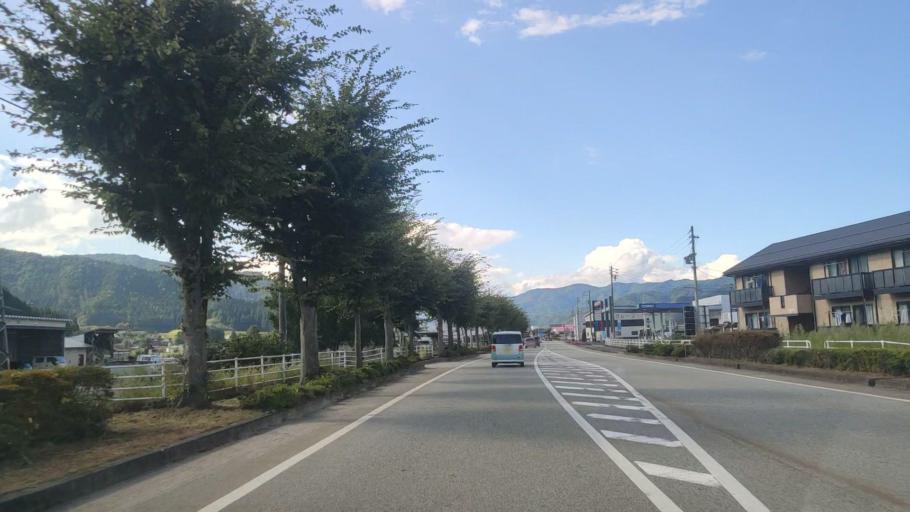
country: JP
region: Gifu
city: Takayama
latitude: 36.2231
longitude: 137.1903
